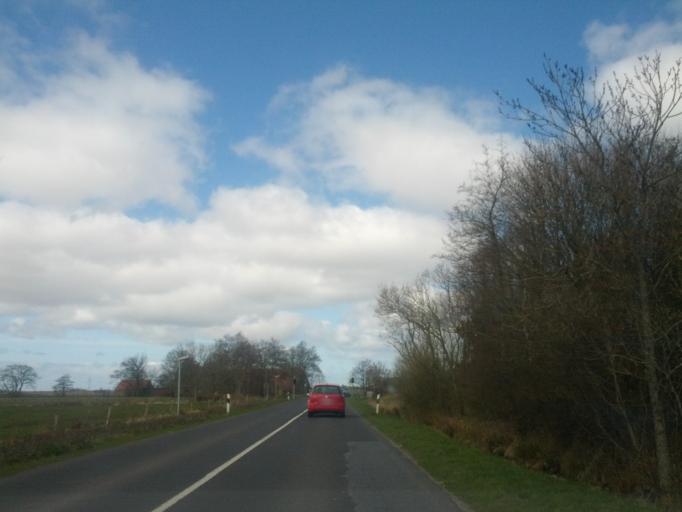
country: DE
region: Lower Saxony
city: Esens
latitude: 53.6540
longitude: 7.6090
